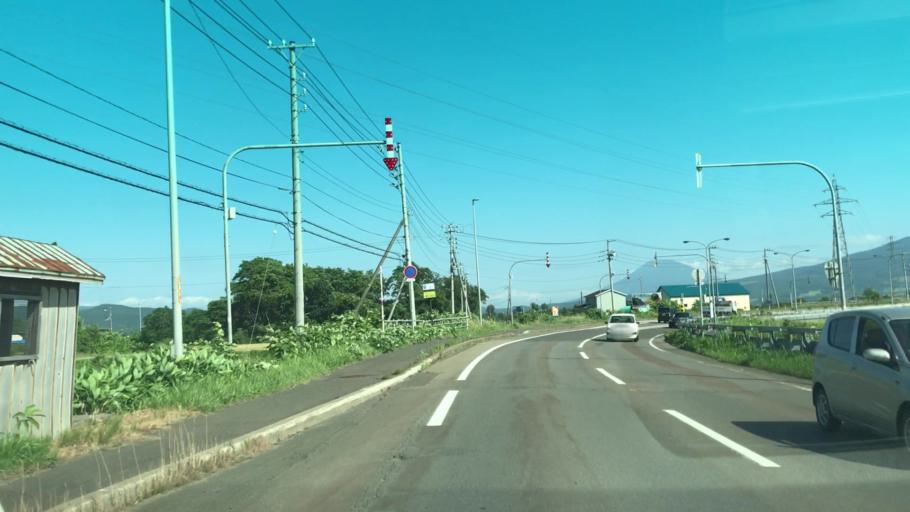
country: JP
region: Hokkaido
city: Iwanai
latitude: 43.0264
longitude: 140.5475
